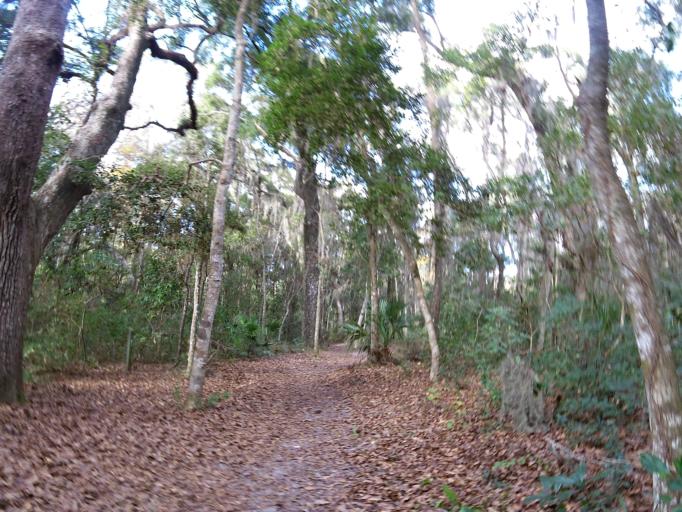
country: US
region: Florida
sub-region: Duval County
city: Atlantic Beach
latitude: 30.3831
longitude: -81.4982
